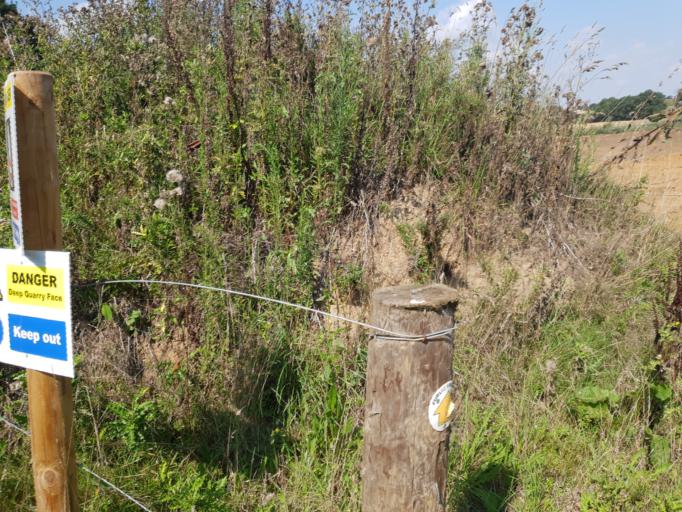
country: GB
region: England
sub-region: Essex
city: Colchester
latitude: 51.9232
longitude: 0.9501
